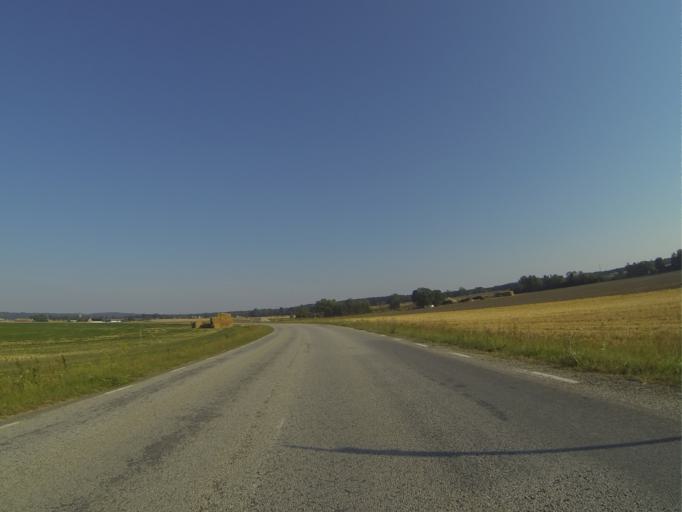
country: SE
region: Skane
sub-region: Lunds Kommun
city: Genarp
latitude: 55.6072
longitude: 13.3680
